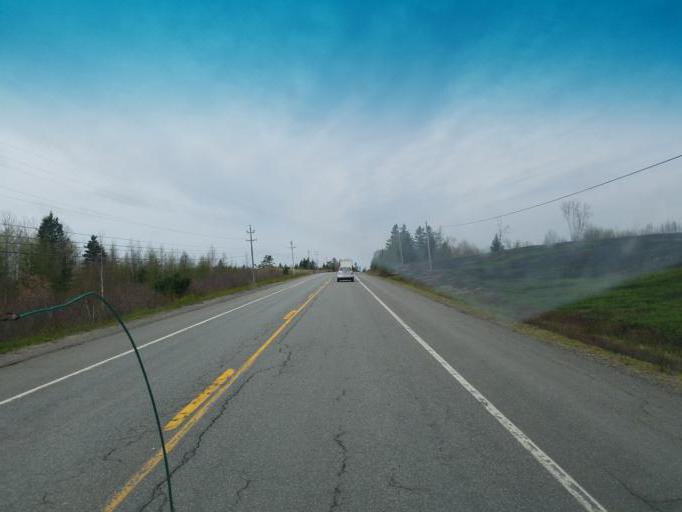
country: US
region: Maine
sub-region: Washington County
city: East Machias
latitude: 44.7559
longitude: -67.2329
